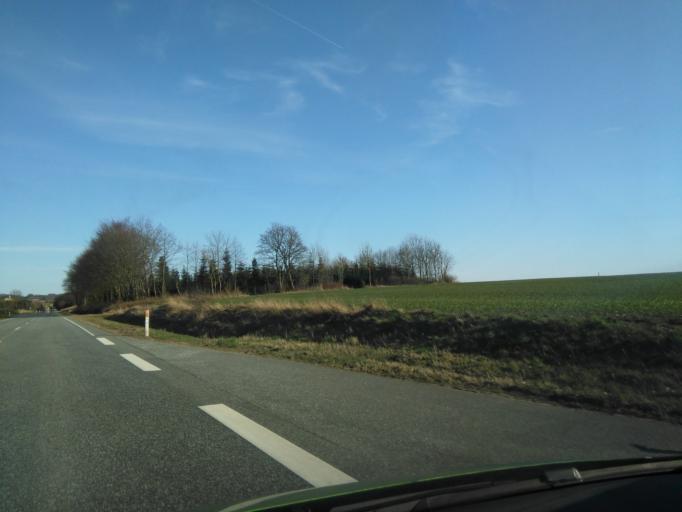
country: DK
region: Central Jutland
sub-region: Horsens Kommune
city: Braedstrup
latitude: 55.9062
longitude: 9.5955
